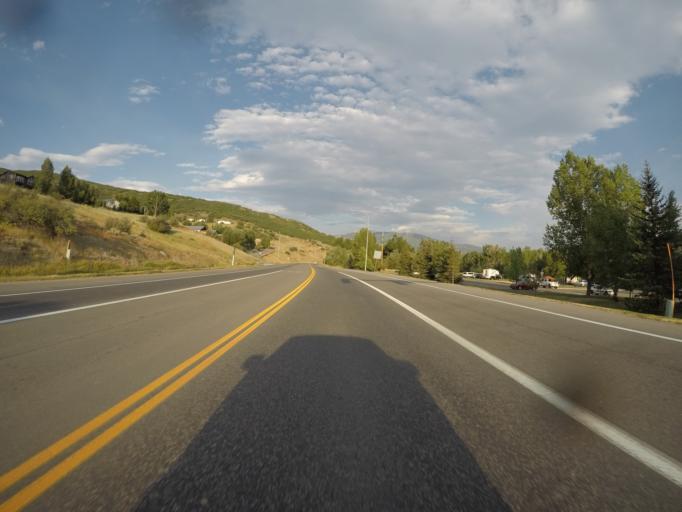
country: US
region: Colorado
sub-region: Routt County
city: Steamboat Springs
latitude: 40.4942
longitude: -106.8499
